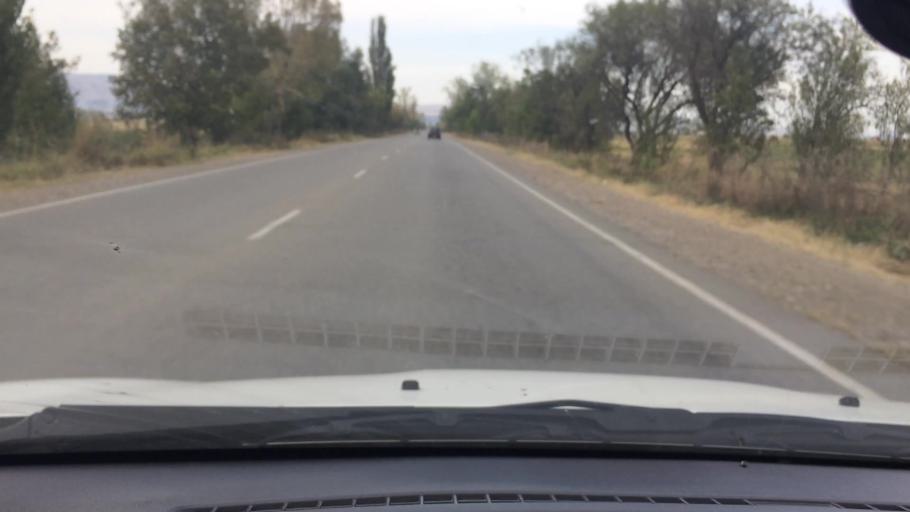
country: GE
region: Kvemo Kartli
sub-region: Marneuli
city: Marneuli
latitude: 41.5514
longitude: 44.7763
